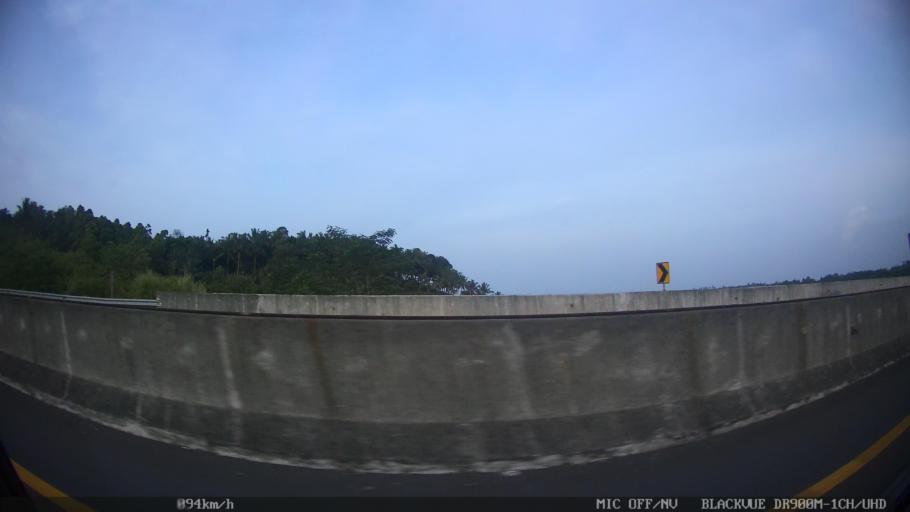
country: ID
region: Lampung
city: Penengahan
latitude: -5.8160
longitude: 105.7367
